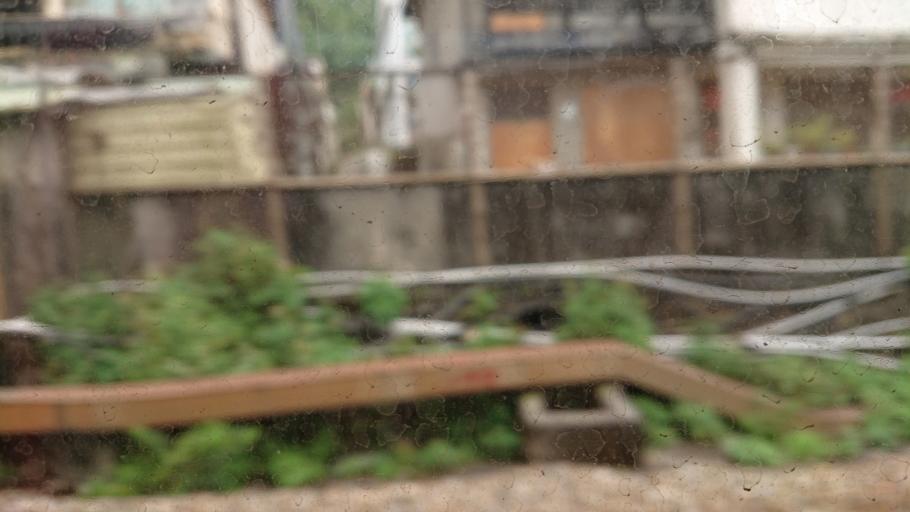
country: TW
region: Taiwan
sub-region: Yilan
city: Yilan
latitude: 24.9410
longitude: 121.8933
